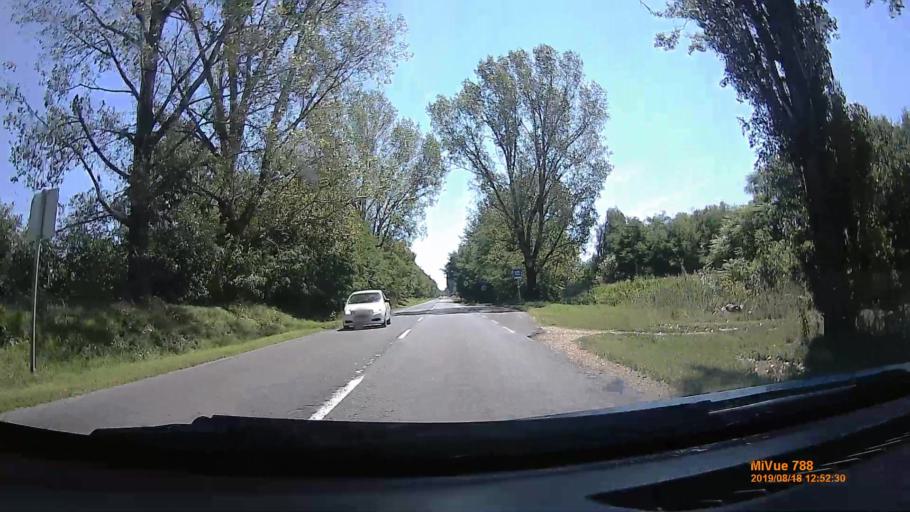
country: HU
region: Fejer
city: Aba
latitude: 47.0621
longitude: 18.5170
